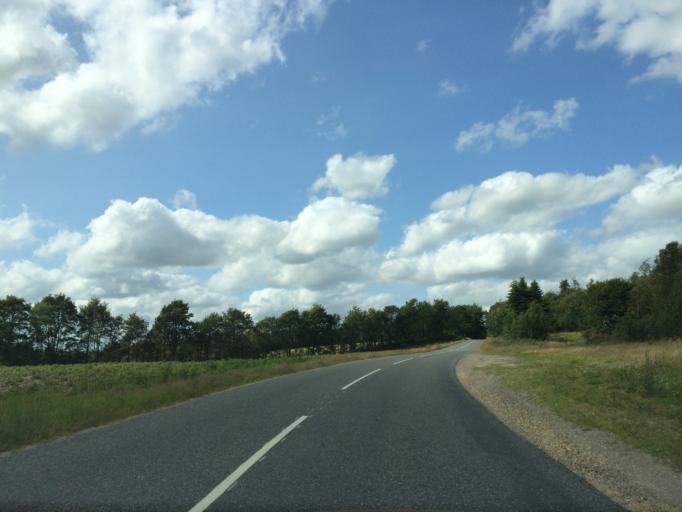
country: DK
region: Central Jutland
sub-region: Skanderborg Kommune
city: Ry
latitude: 56.1955
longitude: 9.7603
